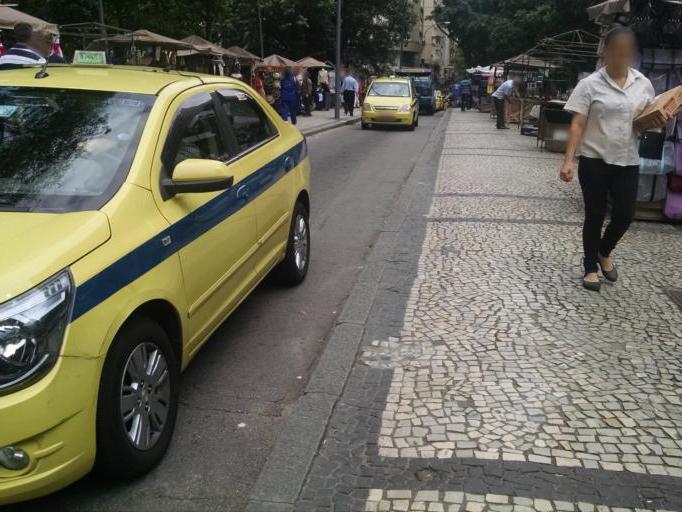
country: BR
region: Rio de Janeiro
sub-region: Rio De Janeiro
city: Rio de Janeiro
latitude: -22.9061
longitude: -43.1755
